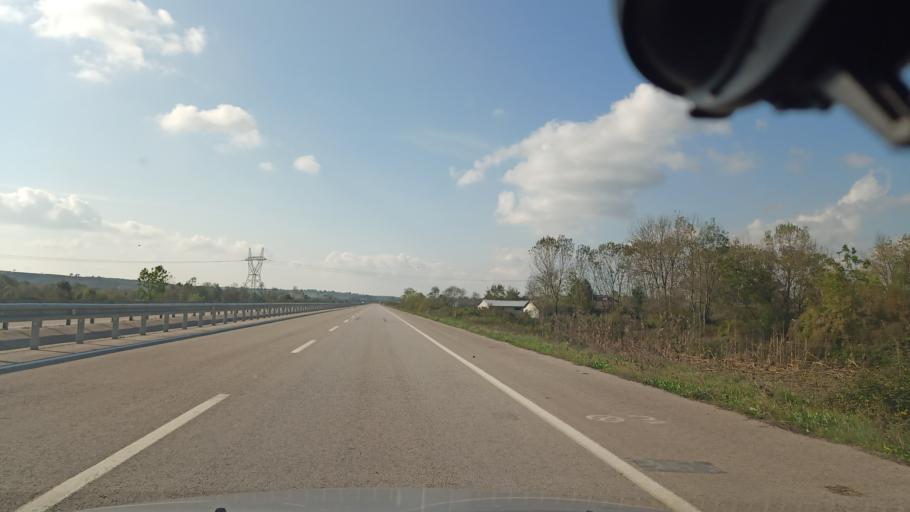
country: TR
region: Sakarya
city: Kaynarca
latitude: 41.0811
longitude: 30.4115
